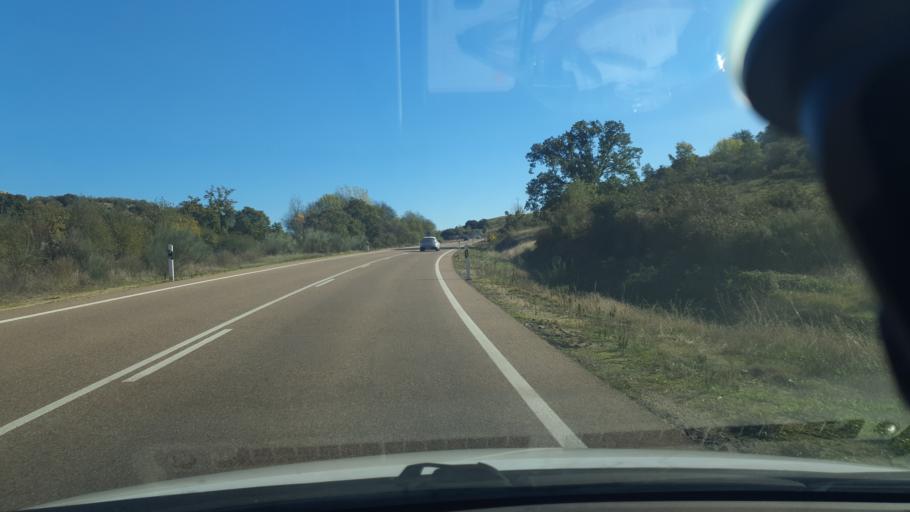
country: ES
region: Castille and Leon
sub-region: Provincia de Avila
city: Poyales del Hoyo
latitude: 40.1581
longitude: -5.1771
